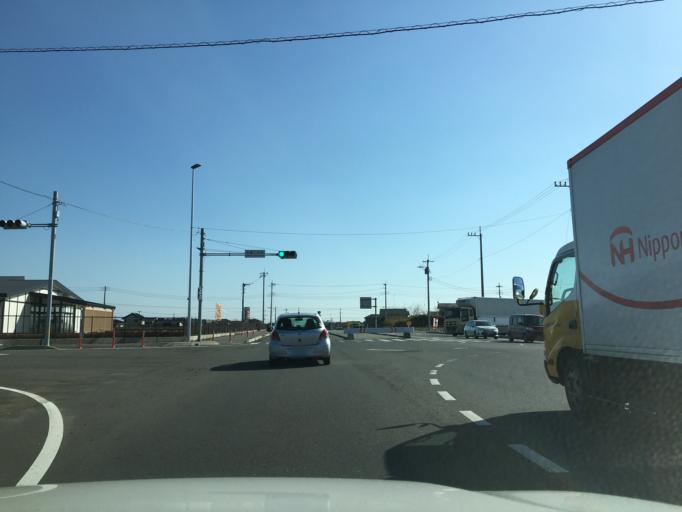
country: JP
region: Ibaraki
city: Omiya
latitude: 36.4837
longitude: 140.3810
